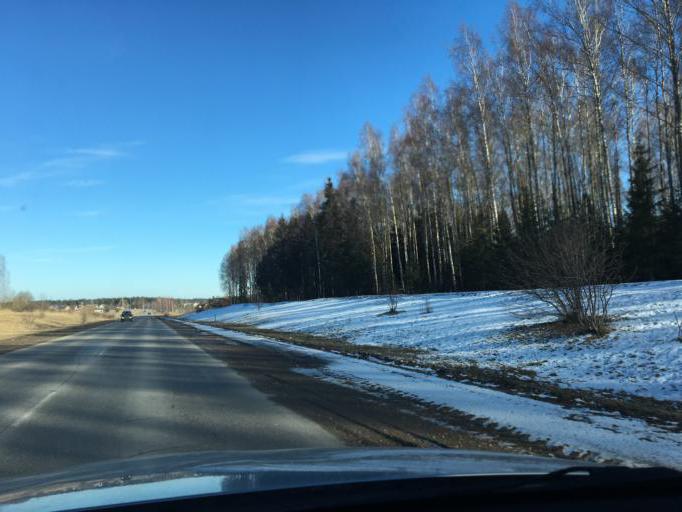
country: LV
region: Jekabpils Rajons
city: Jekabpils
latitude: 56.4864
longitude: 25.8619
